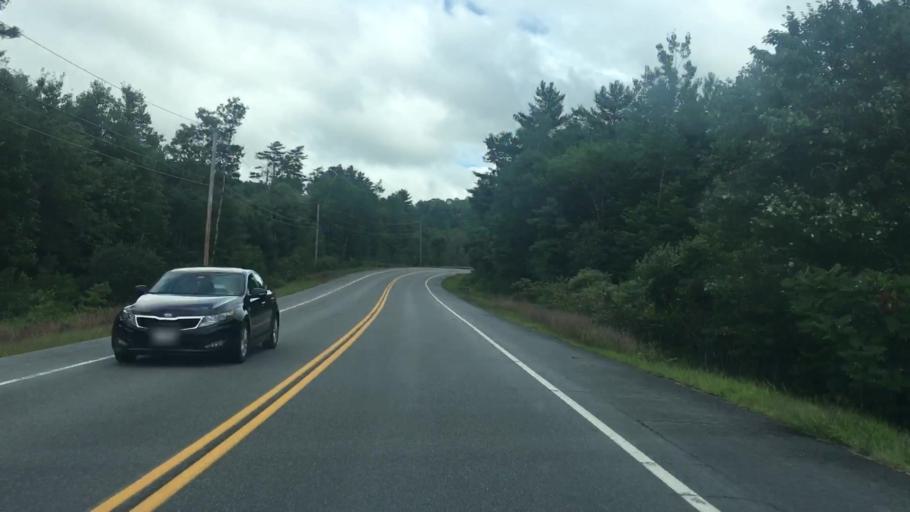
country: US
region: Maine
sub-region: York County
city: Cornish
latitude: 43.7557
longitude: -70.8140
